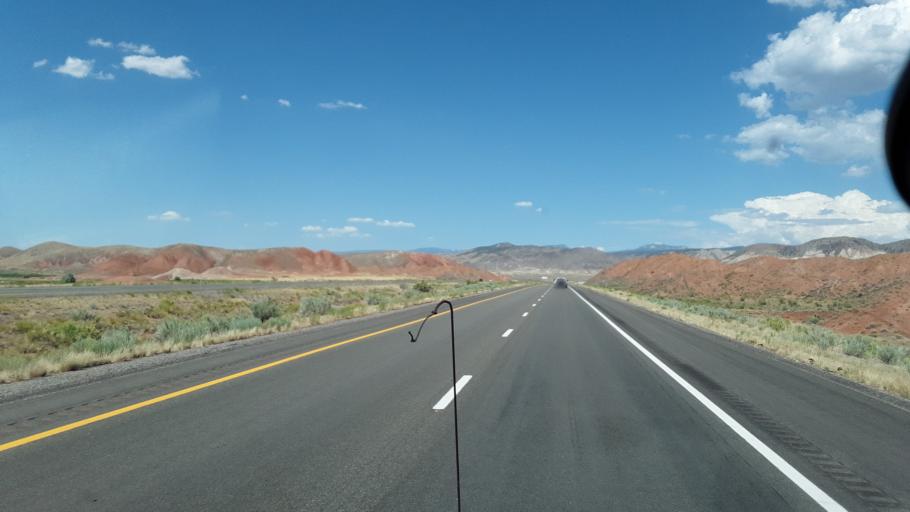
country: US
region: Utah
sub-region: Sevier County
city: Aurora
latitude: 38.9075
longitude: -111.8963
